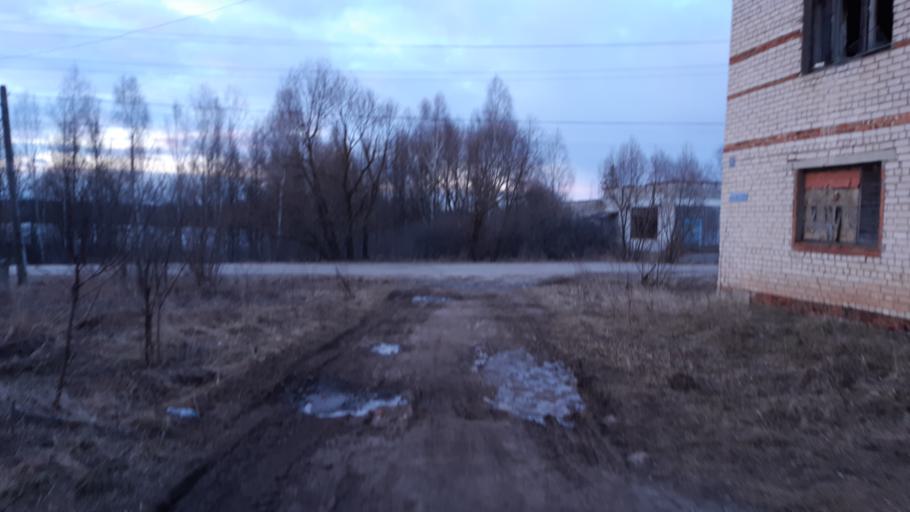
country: RU
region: Vladimir
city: Nikologory
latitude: 56.0950
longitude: 41.9392
